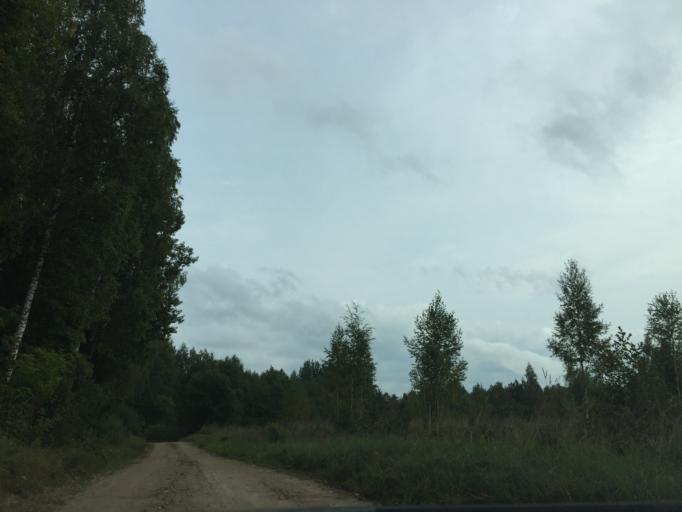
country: LV
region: Dagda
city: Dagda
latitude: 56.2095
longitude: 27.8050
